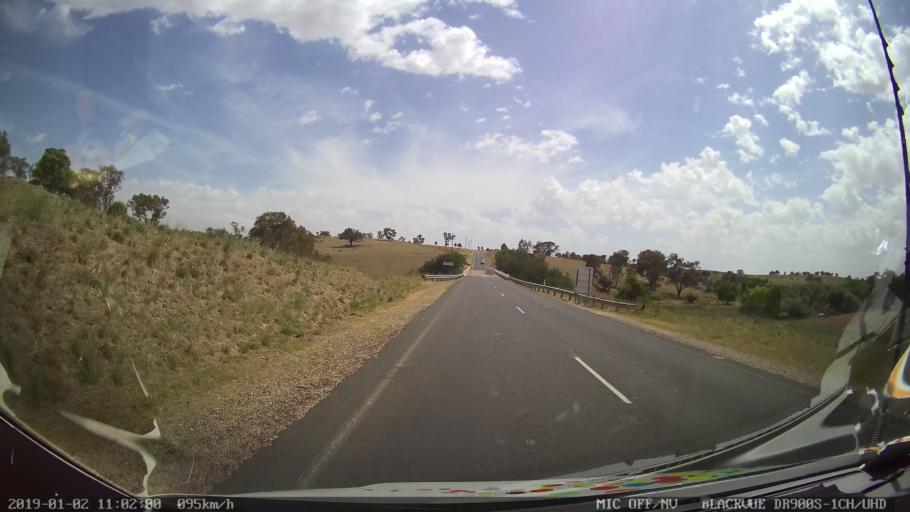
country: AU
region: New South Wales
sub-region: Young
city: Young
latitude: -34.5911
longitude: 148.3238
